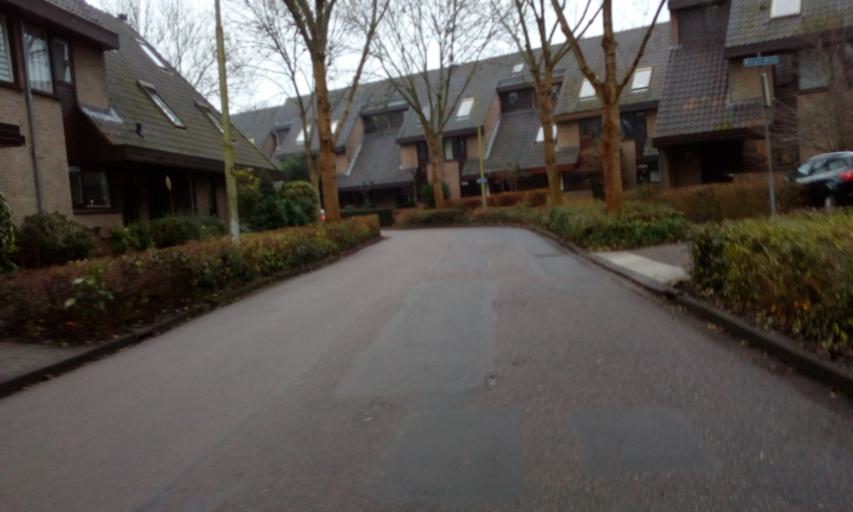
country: NL
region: South Holland
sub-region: Gemeente Pijnacker-Nootdorp
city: Pijnacker
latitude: 52.0110
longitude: 4.4349
